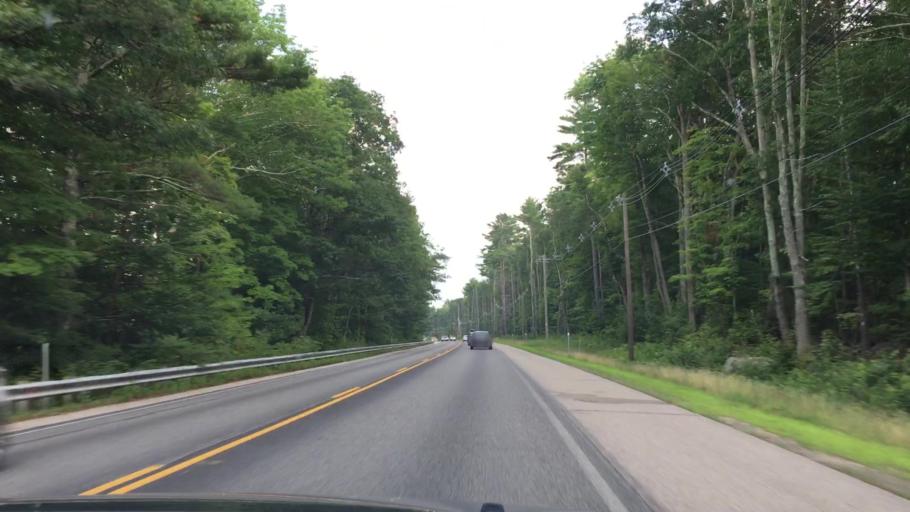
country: US
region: New Hampshire
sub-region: Strafford County
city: Farmington
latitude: 43.3801
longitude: -71.0680
